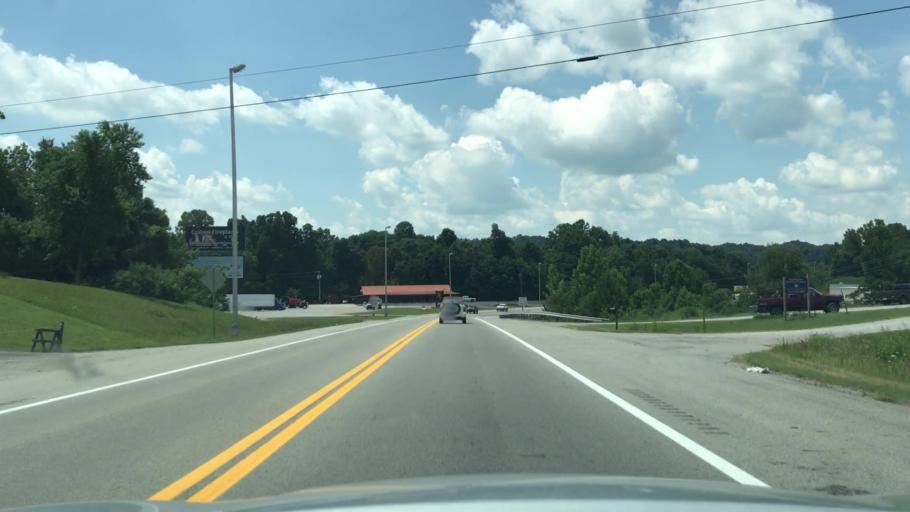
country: US
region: Tennessee
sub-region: Pickett County
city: Byrdstown
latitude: 36.5776
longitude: -85.1373
